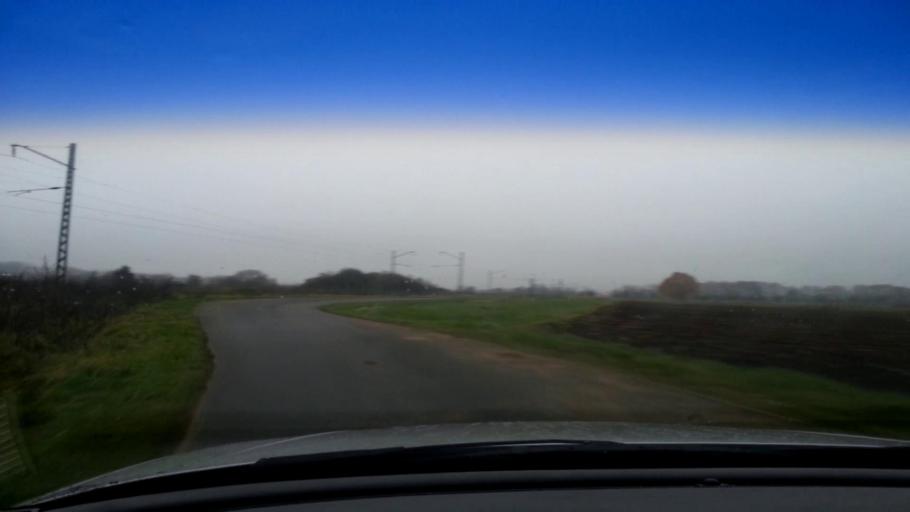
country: DE
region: Bavaria
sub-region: Upper Franconia
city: Hallstadt
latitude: 49.9401
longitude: 10.8862
